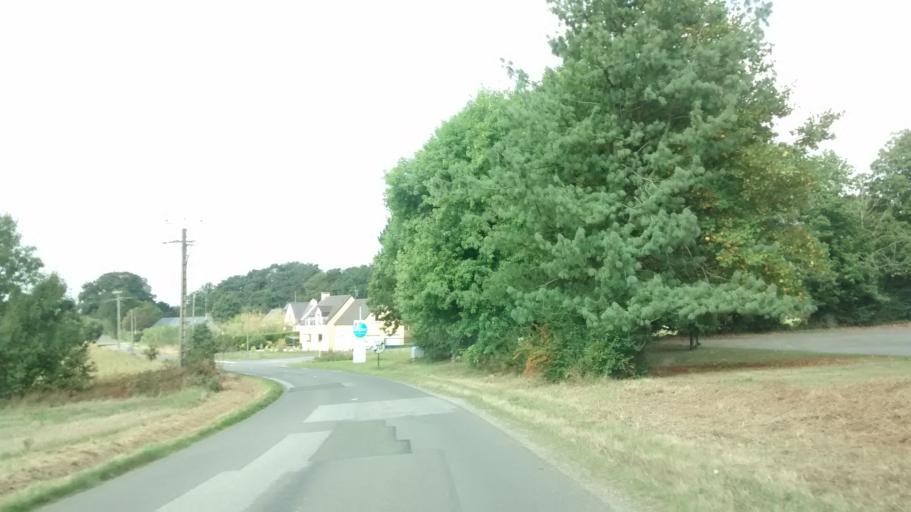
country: FR
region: Brittany
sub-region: Departement d'Ille-et-Vilaine
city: Chatillon-en-Vendelais
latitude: 48.2280
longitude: -1.1943
